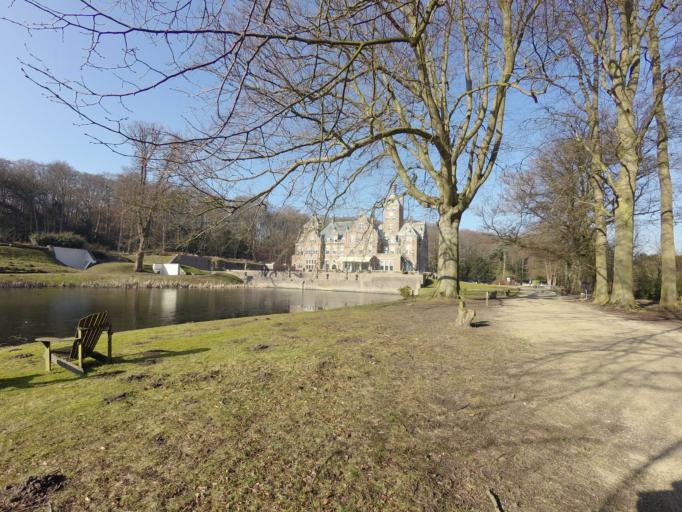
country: NL
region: North Holland
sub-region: Gemeente Bloemendaal
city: Bloemendaal
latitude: 52.4334
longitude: 4.6264
